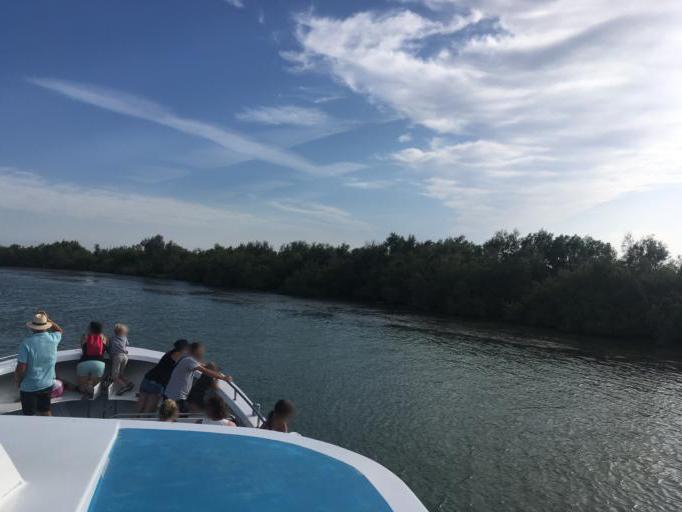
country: FR
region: Provence-Alpes-Cote d'Azur
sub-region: Departement des Bouches-du-Rhone
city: Saintes-Maries-de-la-Mer
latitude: 43.4744
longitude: 4.3872
